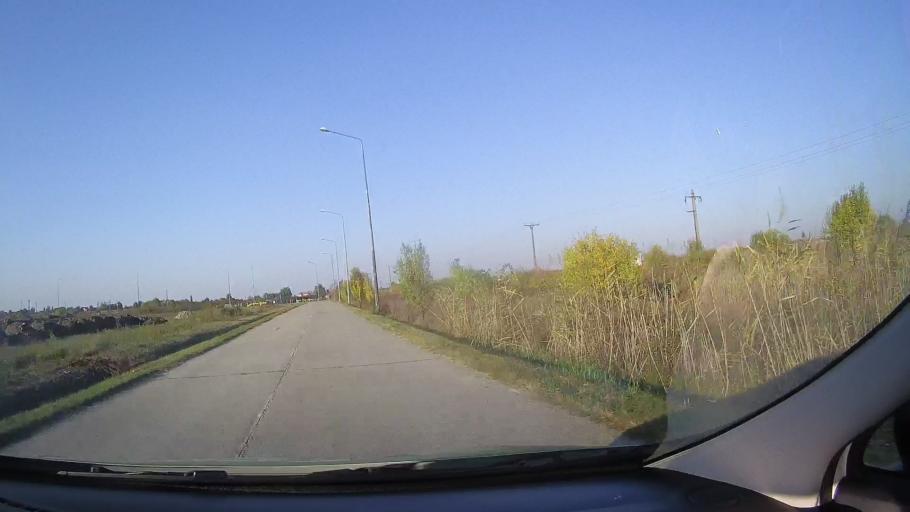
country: RO
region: Bihor
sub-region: Comuna Bors
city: Santion
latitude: 47.1086
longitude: 21.8316
